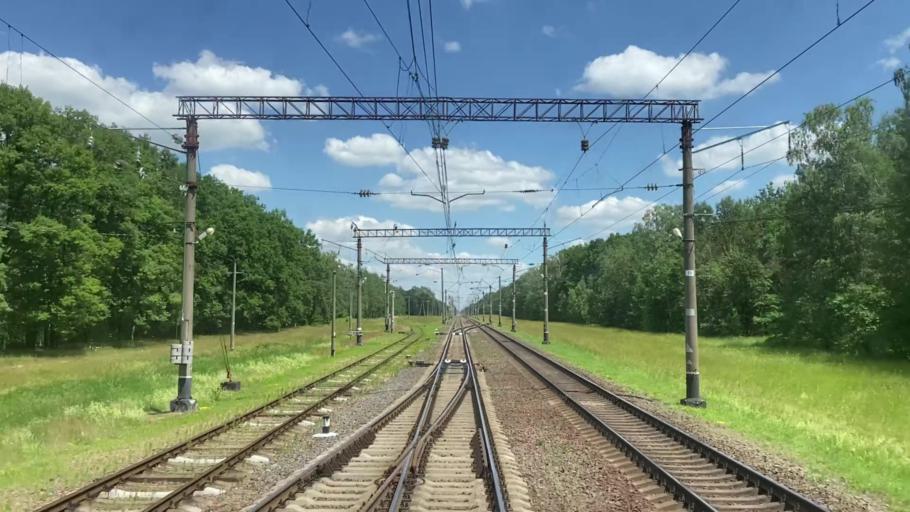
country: BY
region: Brest
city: Pruzhany
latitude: 52.4787
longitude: 24.5495
